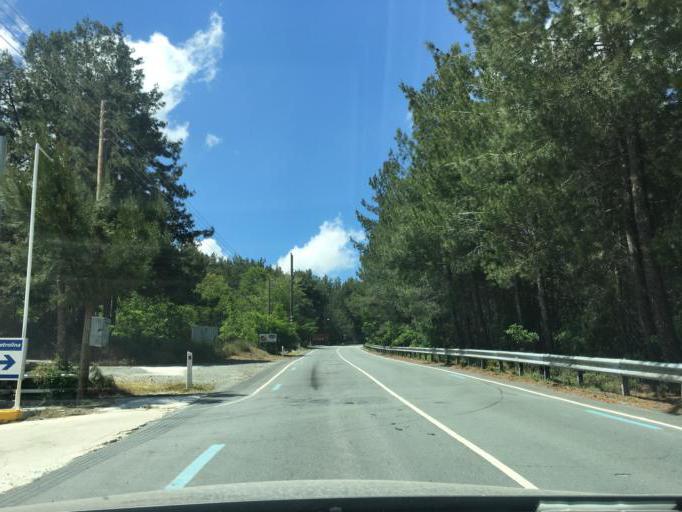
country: CY
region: Limassol
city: Kyperounta
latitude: 34.9402
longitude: 32.9312
